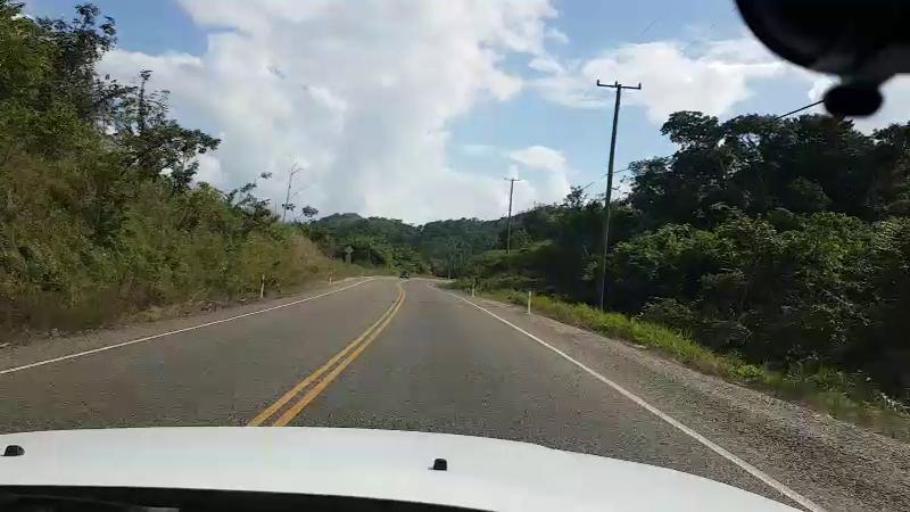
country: BZ
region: Cayo
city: Belmopan
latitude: 17.2265
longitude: -88.7790
